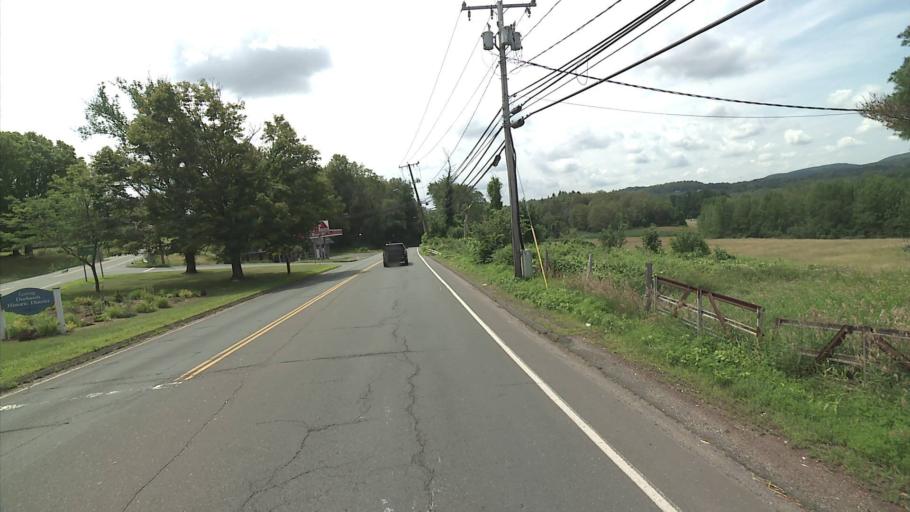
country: US
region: Connecticut
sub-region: Middlesex County
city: Durham
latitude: 41.4656
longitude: -72.6790
